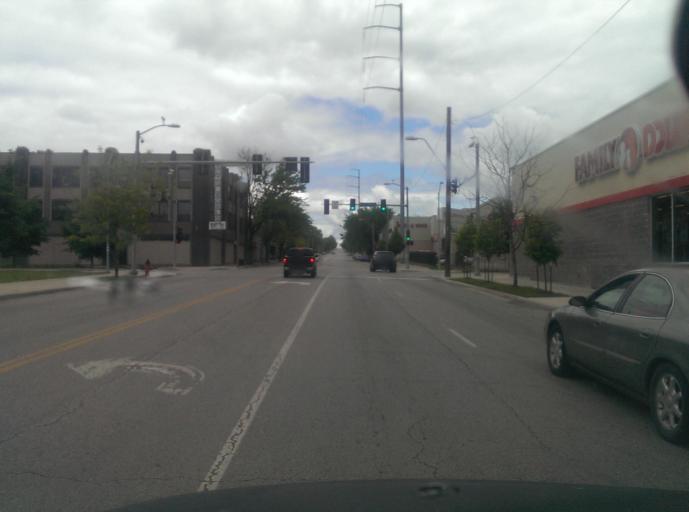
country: US
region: Kansas
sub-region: Johnson County
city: Westwood
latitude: 39.0429
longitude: -94.5729
